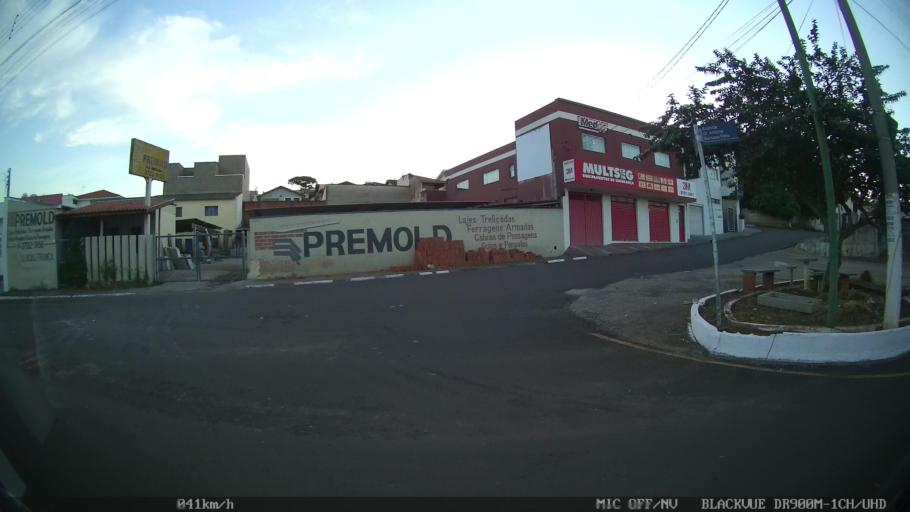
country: BR
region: Sao Paulo
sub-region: Franca
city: Franca
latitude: -20.5405
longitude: -47.4082
